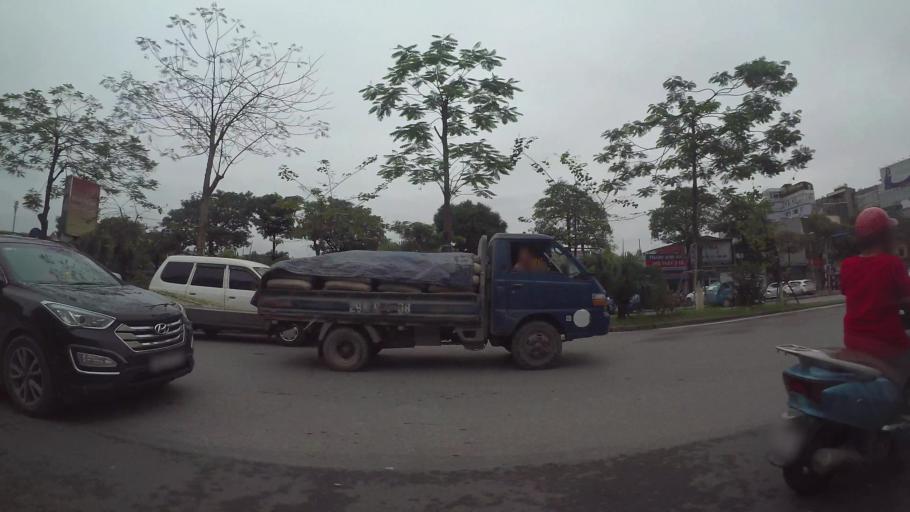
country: VN
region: Ha Noi
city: Hai BaTrung
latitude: 21.0092
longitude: 105.8552
